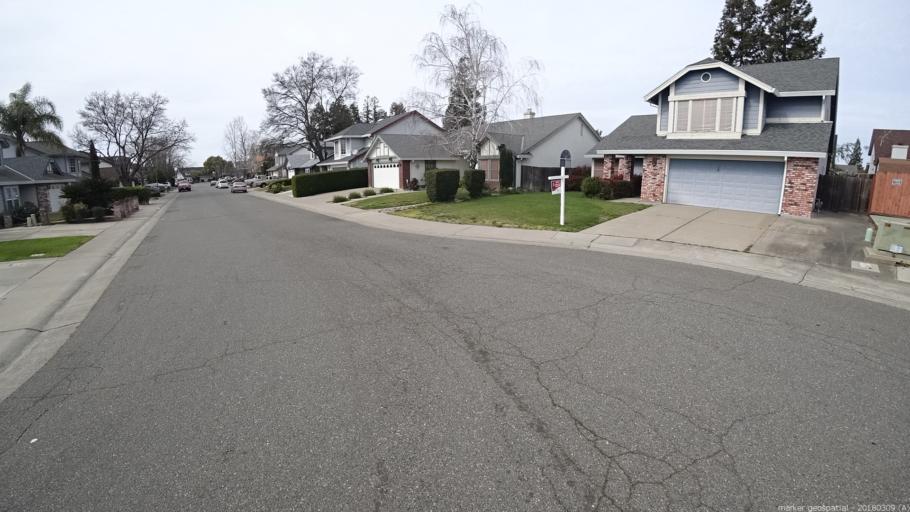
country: US
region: California
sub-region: Sacramento County
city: Vineyard
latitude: 38.4646
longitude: -121.3822
